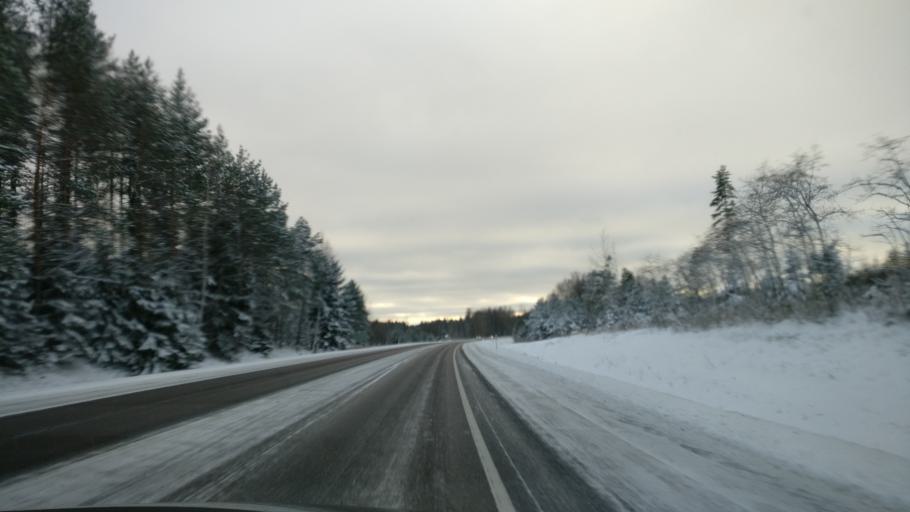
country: FI
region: Paijanne Tavastia
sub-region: Lahti
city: Heinola
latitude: 61.3259
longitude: 26.1573
